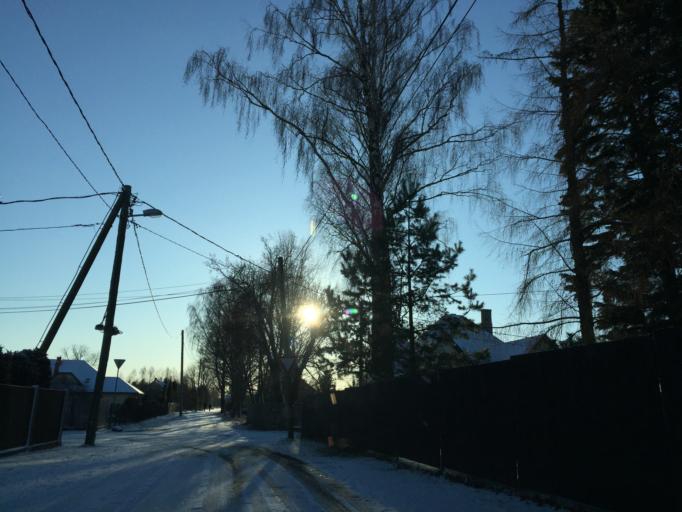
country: LV
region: Marupe
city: Marupe
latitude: 56.9121
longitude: 24.0545
